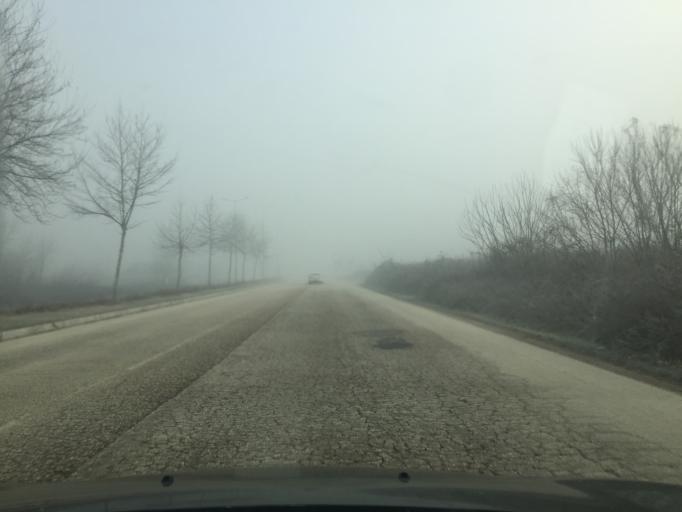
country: TR
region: Duzce
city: Duzce
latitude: 40.8608
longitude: 31.2121
